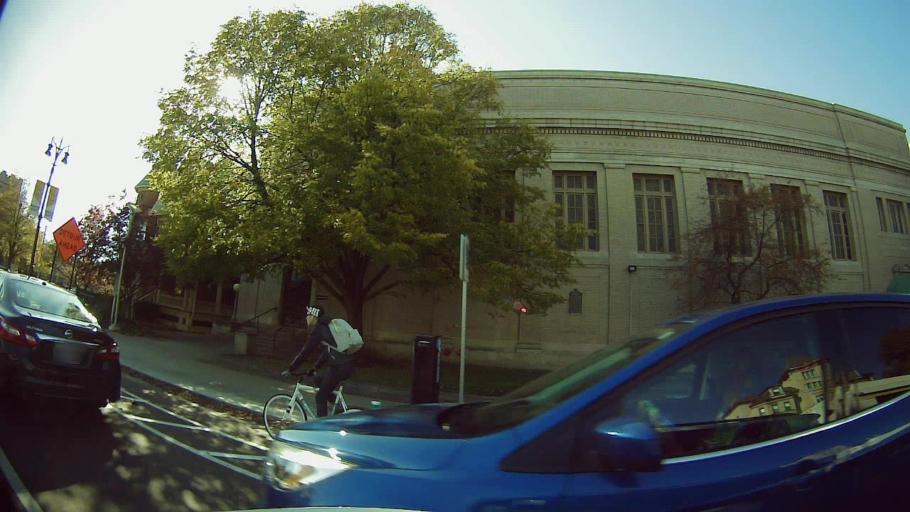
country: US
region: Michigan
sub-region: Wayne County
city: Detroit
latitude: 42.3545
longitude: -83.0658
